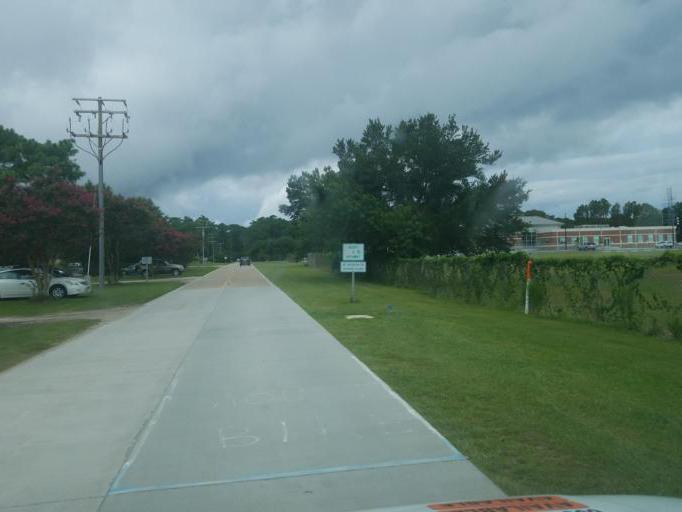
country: US
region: North Carolina
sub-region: Dare County
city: Manteo
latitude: 35.9180
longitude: -75.7027
